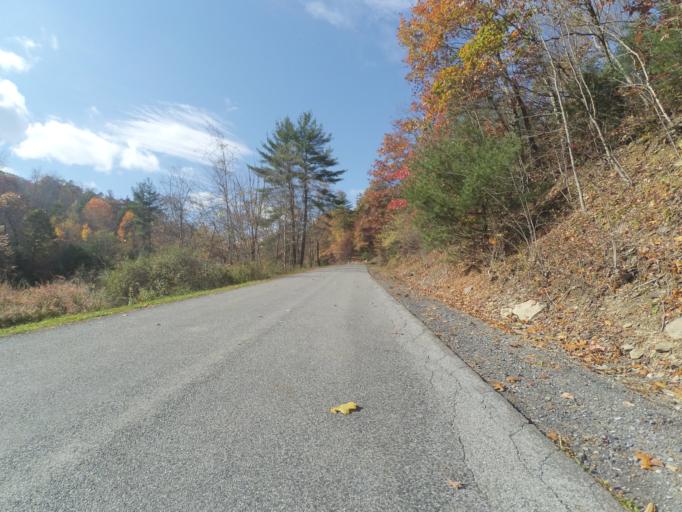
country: US
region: Pennsylvania
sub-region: Centre County
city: Park Forest Village
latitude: 40.8616
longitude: -77.9590
